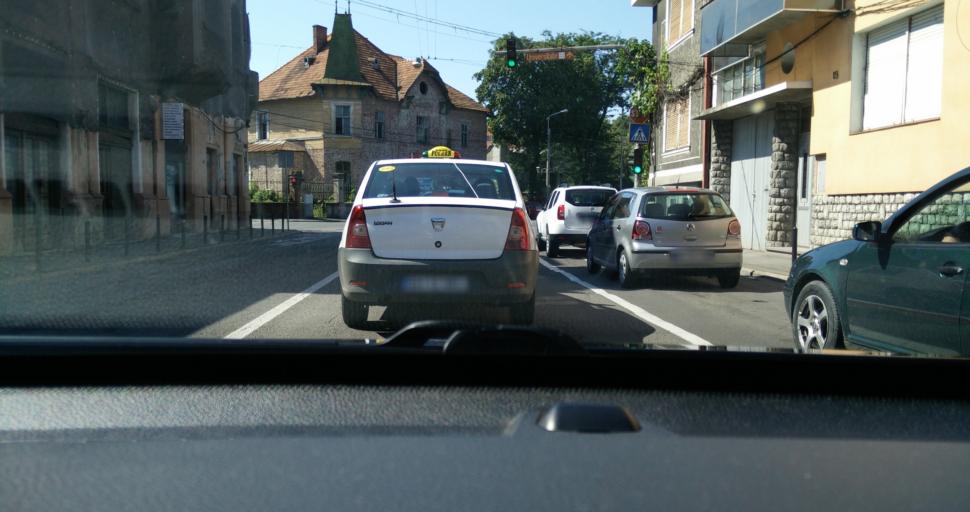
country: RO
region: Bihor
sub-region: Comuna Biharea
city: Oradea
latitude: 47.0507
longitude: 21.9264
